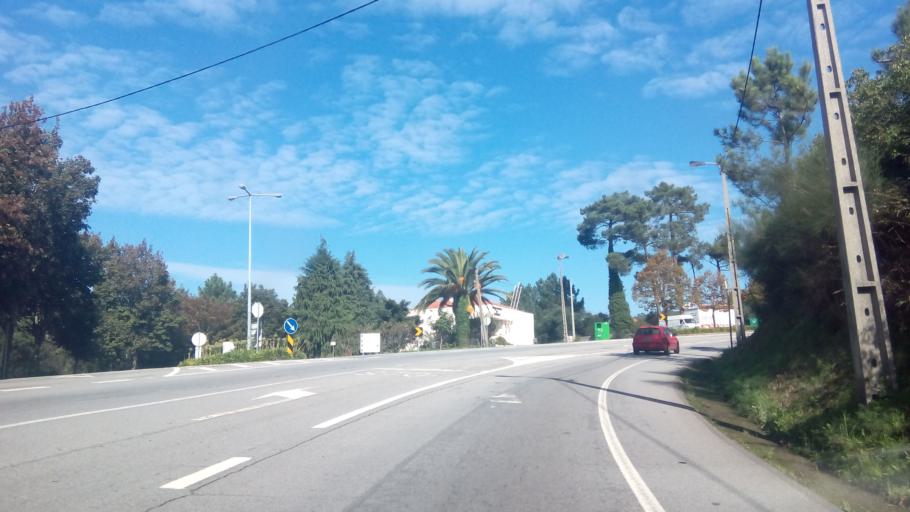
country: PT
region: Porto
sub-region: Paredes
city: Gandra
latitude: 41.1968
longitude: -8.4253
